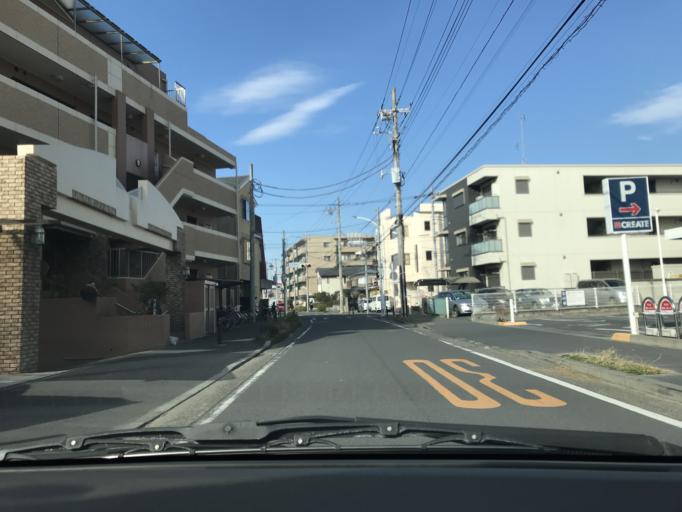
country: JP
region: Tokyo
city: Chofugaoka
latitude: 35.6141
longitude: 139.5953
